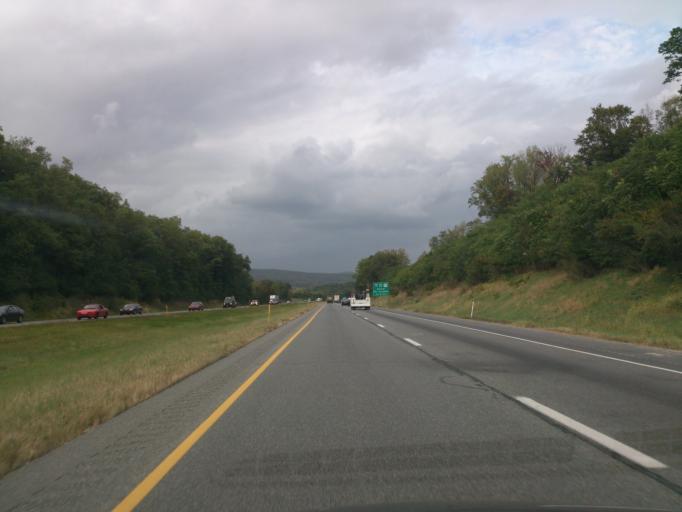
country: US
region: Pennsylvania
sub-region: Lancaster County
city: Reamstown
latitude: 40.1955
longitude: -76.1226
